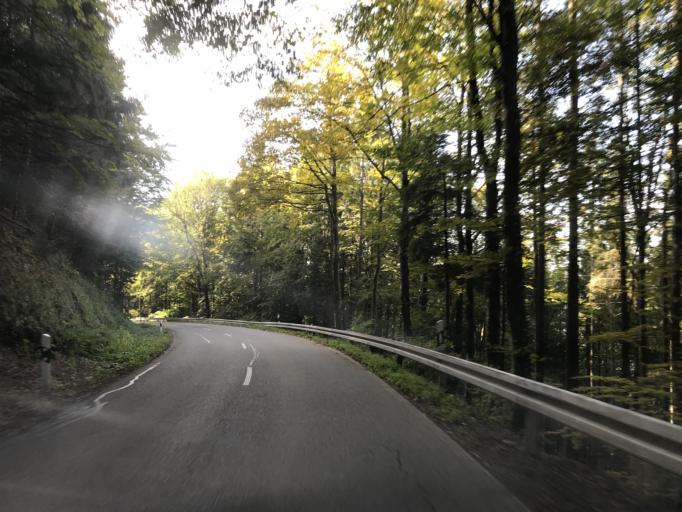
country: DE
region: Baden-Wuerttemberg
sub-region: Freiburg Region
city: Wehr
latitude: 47.6393
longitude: 7.9369
